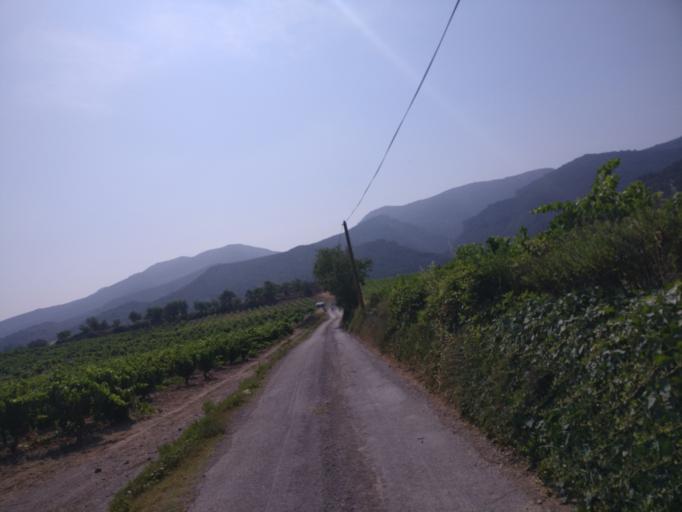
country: FR
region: Languedoc-Roussillon
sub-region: Departement des Pyrenees-Orientales
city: Salses-le-Chateau
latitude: 42.9374
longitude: 2.8148
